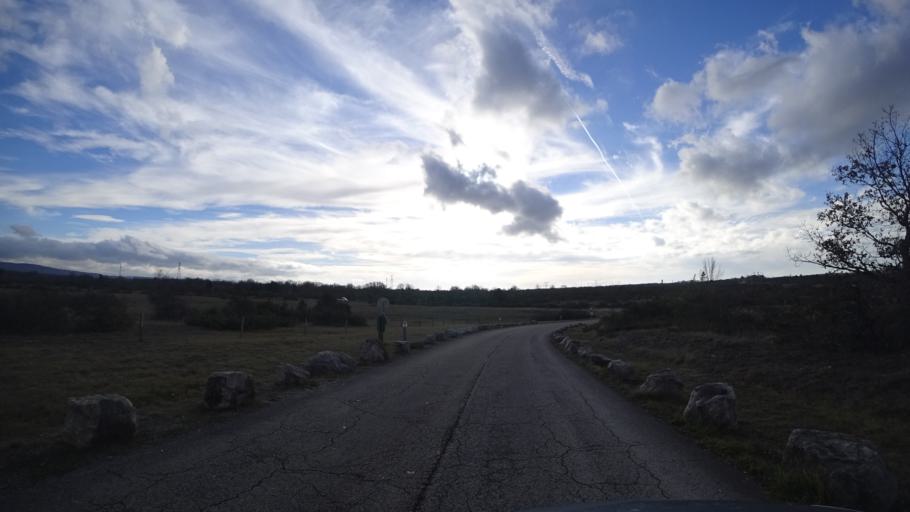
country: FR
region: Midi-Pyrenees
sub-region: Departement de l'Aveyron
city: La Loubiere
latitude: 44.4206
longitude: 2.6670
